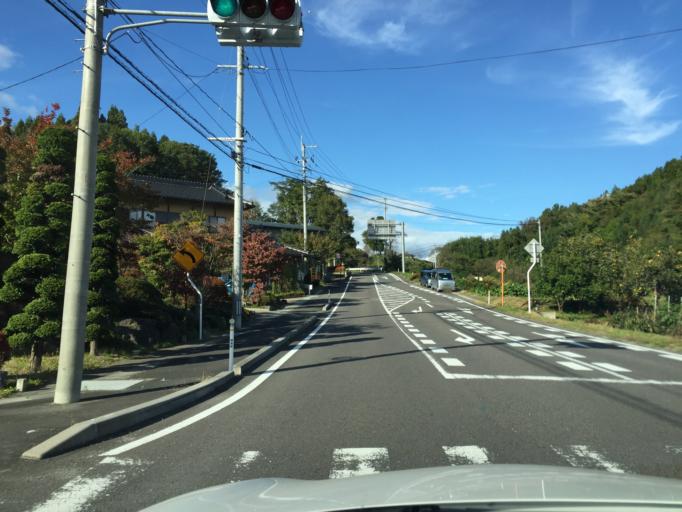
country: JP
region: Fukushima
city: Ishikawa
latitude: 37.2083
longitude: 140.4543
